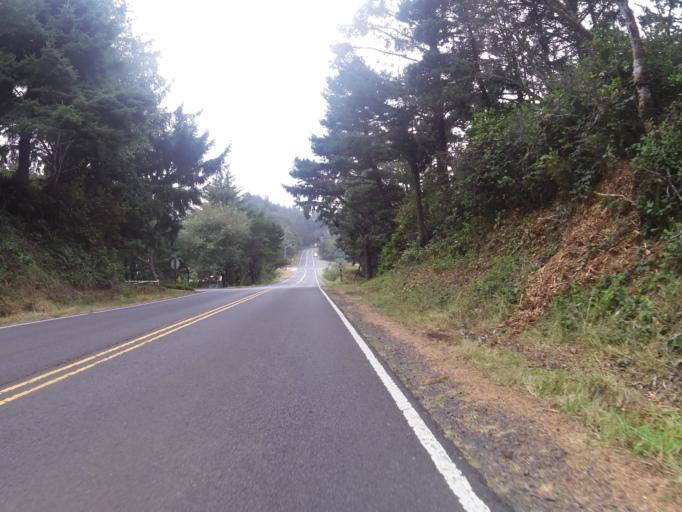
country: US
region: Oregon
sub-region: Lincoln County
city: Newport
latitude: 44.6601
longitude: -124.0567
